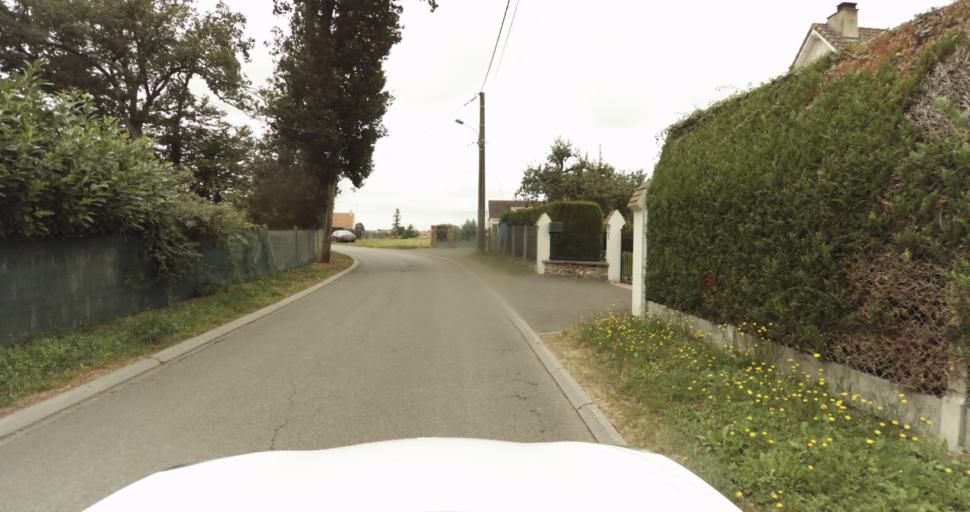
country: FR
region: Haute-Normandie
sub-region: Departement de l'Eure
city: Saint-Sebastien-de-Morsent
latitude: 49.0066
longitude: 1.0665
